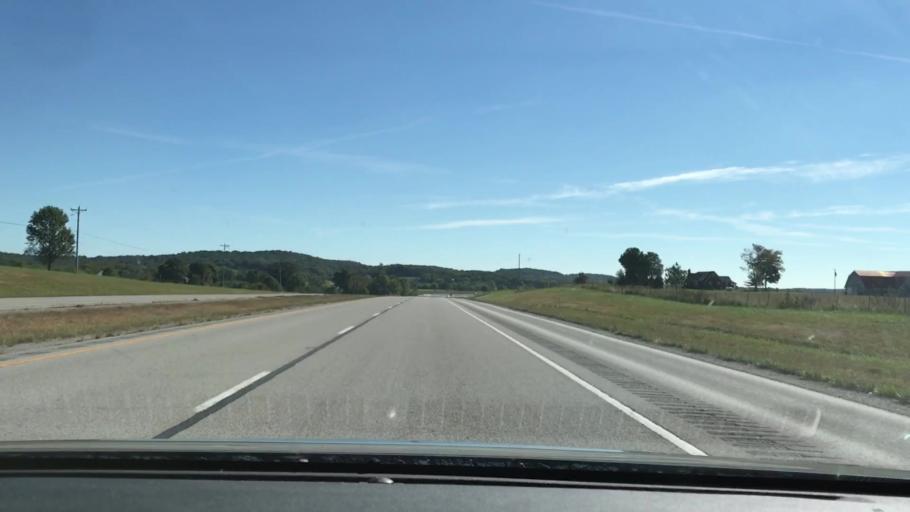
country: US
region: Kentucky
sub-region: Todd County
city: Elkton
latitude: 36.8407
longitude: -87.2533
